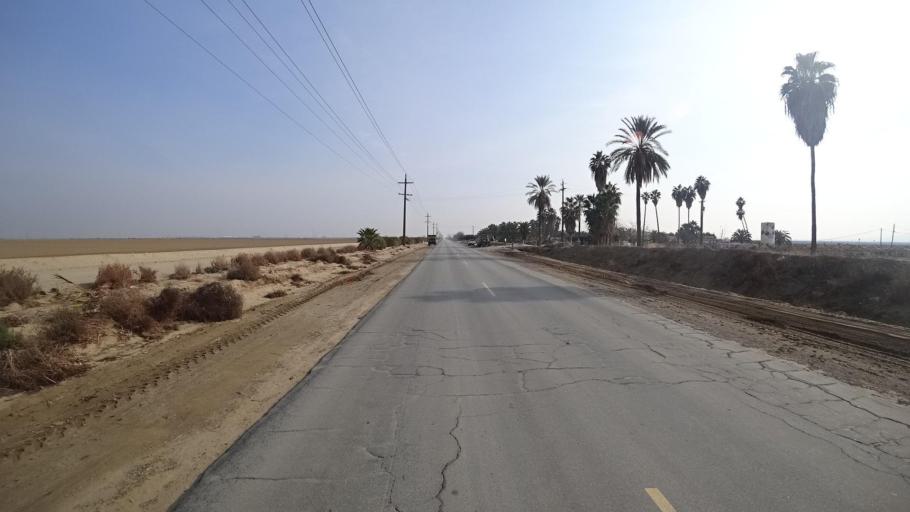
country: US
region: California
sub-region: Kern County
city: Greenfield
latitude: 35.0951
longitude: -119.0299
